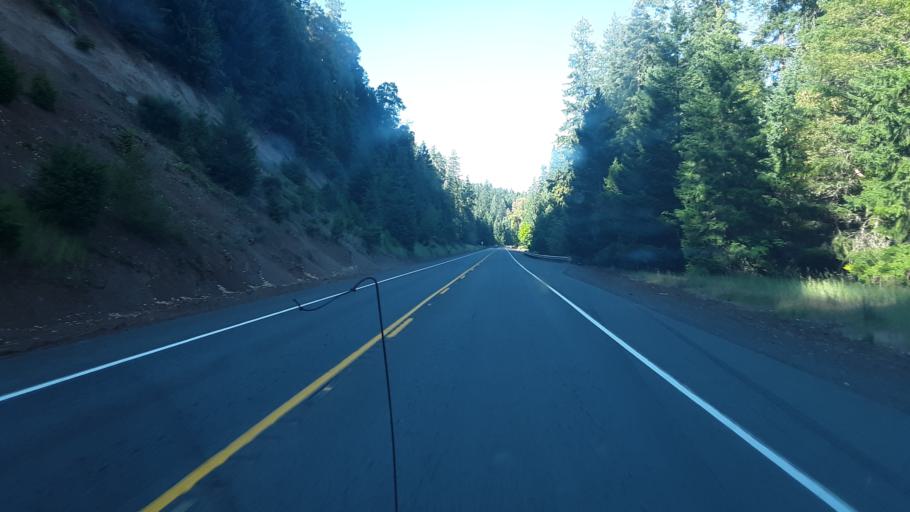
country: US
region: Oregon
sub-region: Jackson County
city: Shady Cove
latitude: 42.6798
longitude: -122.6169
